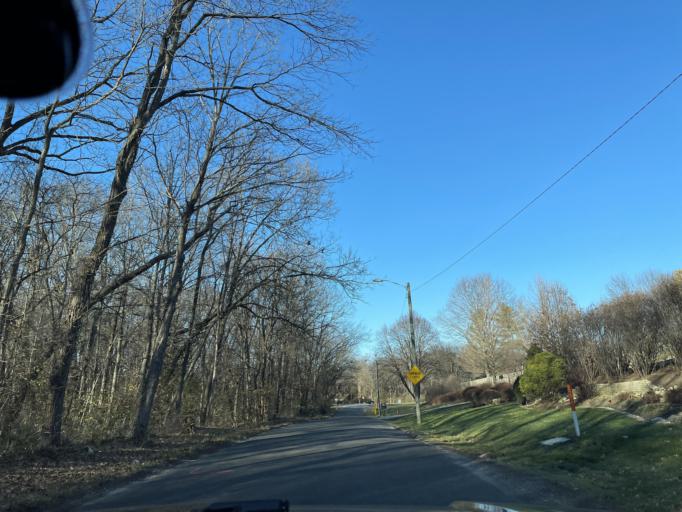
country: US
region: Illinois
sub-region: Sangamon County
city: Leland Grove
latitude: 39.7992
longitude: -89.7155
